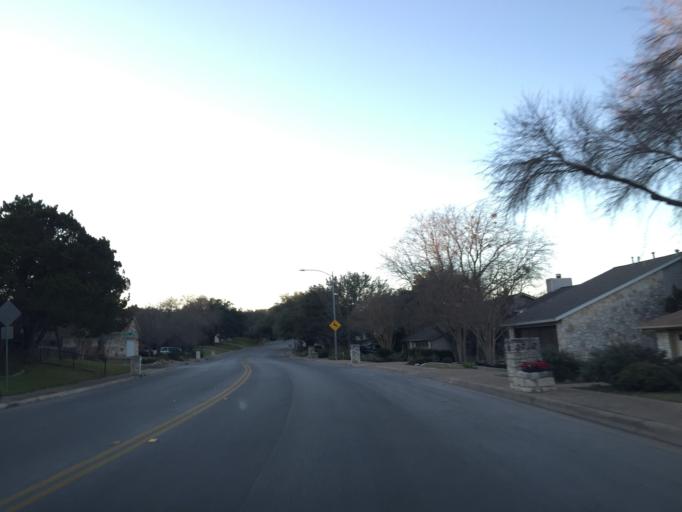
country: US
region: Texas
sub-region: Williamson County
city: Jollyville
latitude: 30.4063
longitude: -97.7599
